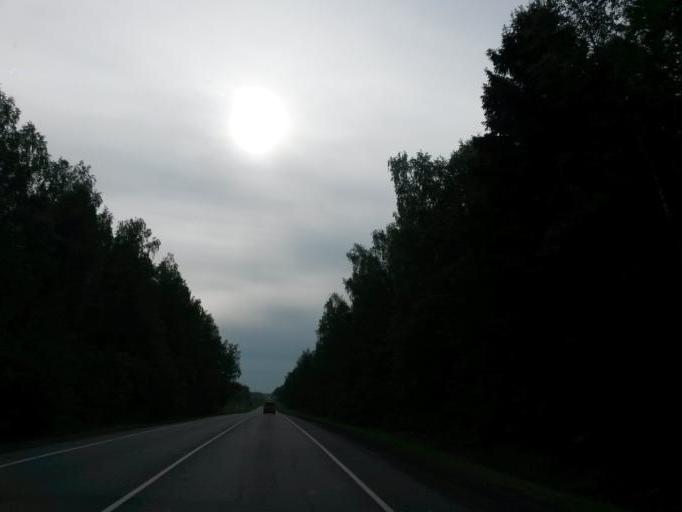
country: RU
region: Moskovskaya
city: Klimovsk
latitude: 55.3313
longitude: 37.6378
